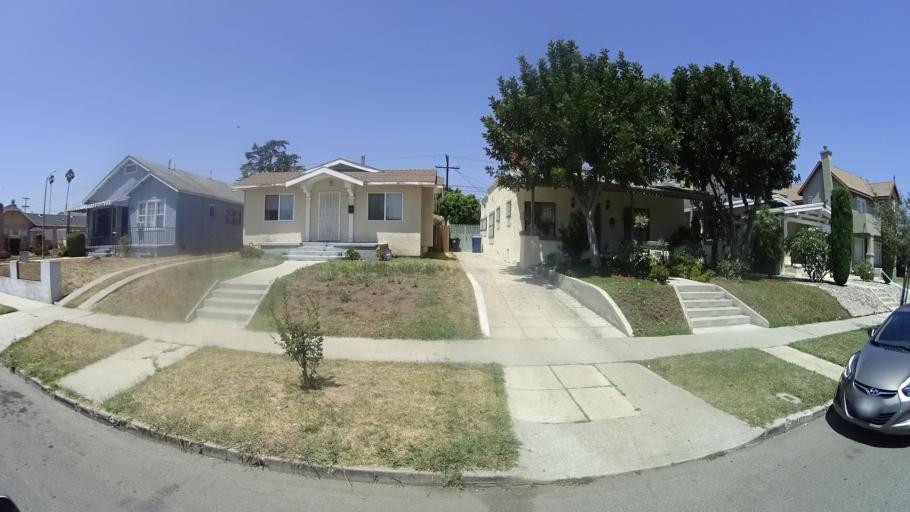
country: US
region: California
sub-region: Los Angeles County
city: View Park-Windsor Hills
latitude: 33.9913
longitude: -118.3237
